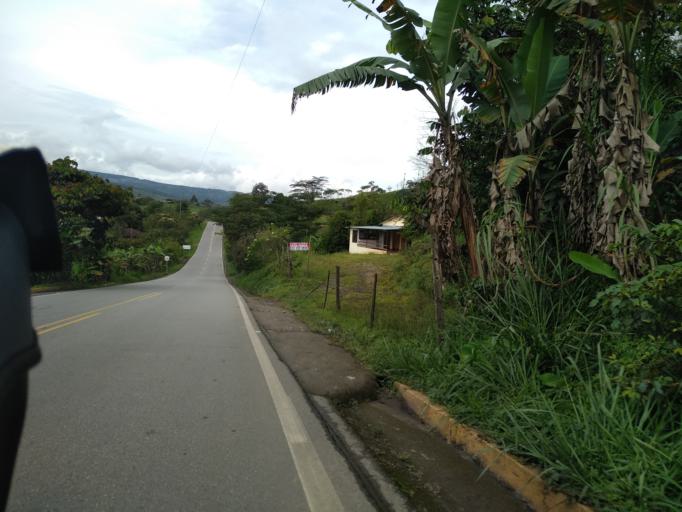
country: CO
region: Santander
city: Suaita
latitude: 6.1297
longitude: -73.3610
